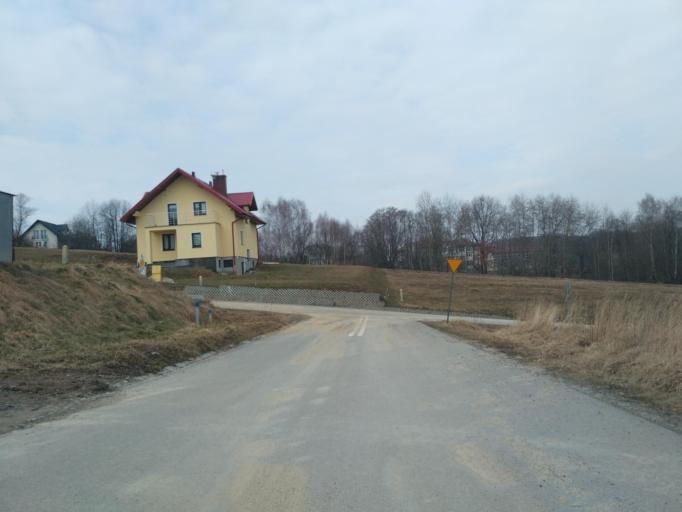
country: PL
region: Subcarpathian Voivodeship
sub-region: Powiat ropczycko-sedziszowski
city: Wielopole Skrzynskie
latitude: 49.9418
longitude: 21.6126
